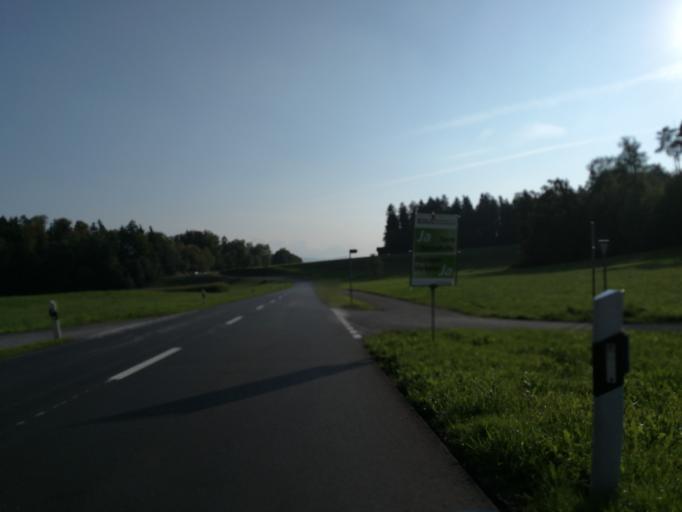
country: CH
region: Zurich
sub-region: Bezirk Meilen
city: Oetwil am See
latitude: 47.2618
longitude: 8.7230
